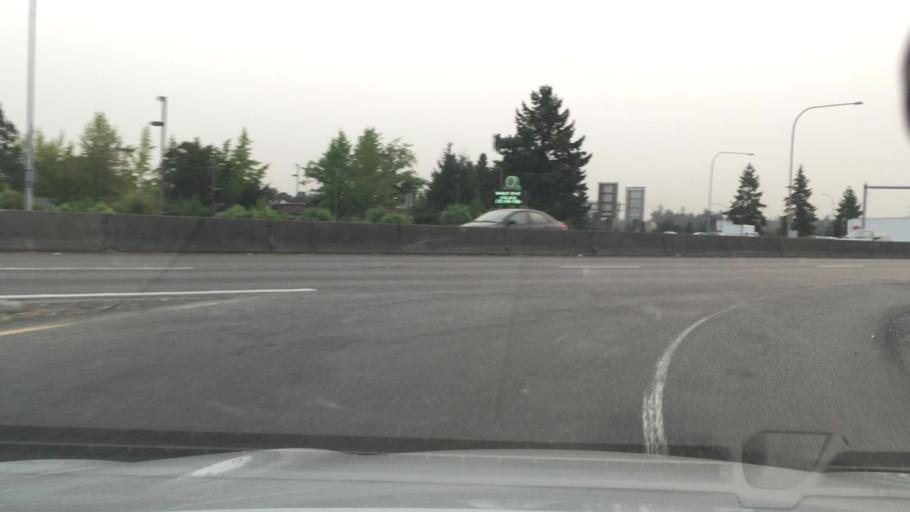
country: US
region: Washington
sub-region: Pierce County
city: McChord Air Force Base
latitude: 47.1638
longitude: -122.4832
